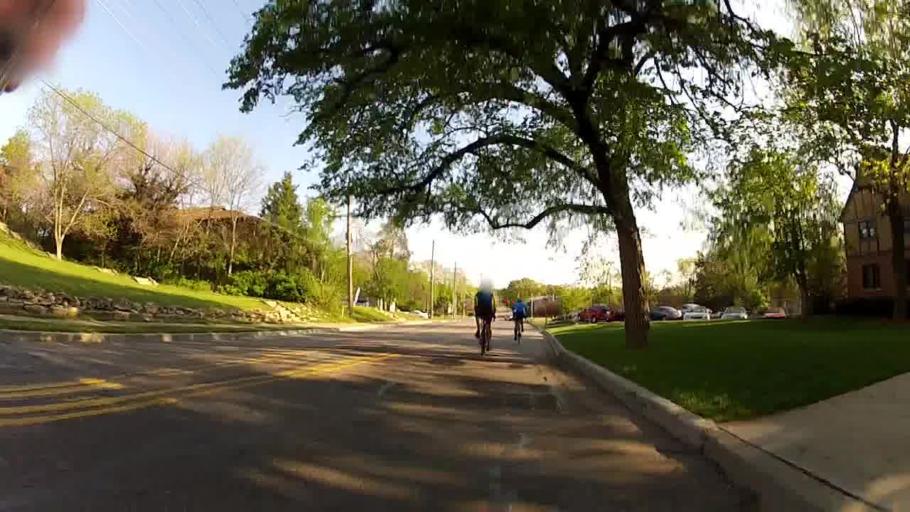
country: US
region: Kansas
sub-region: Riley County
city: Manhattan
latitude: 39.1848
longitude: -96.5888
